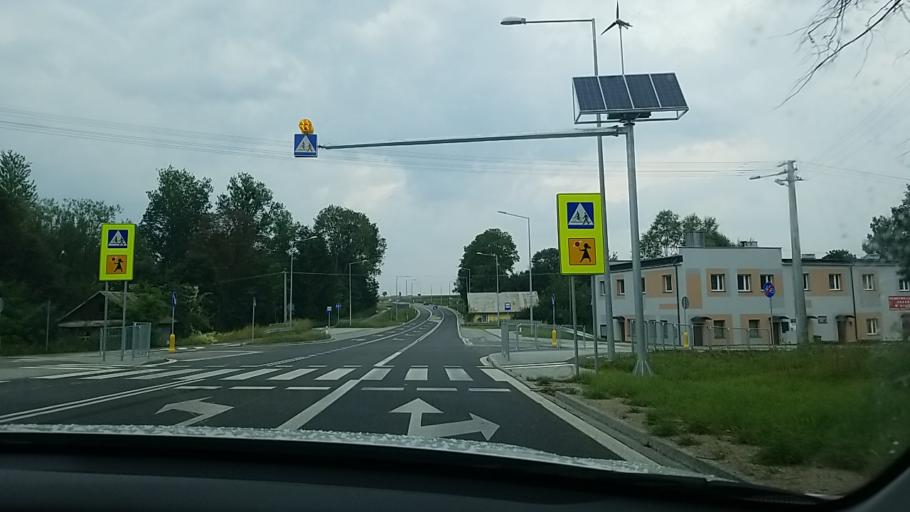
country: PL
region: Lublin Voivodeship
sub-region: Powiat lubelski
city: Wysokie
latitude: 50.9566
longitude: 22.6787
